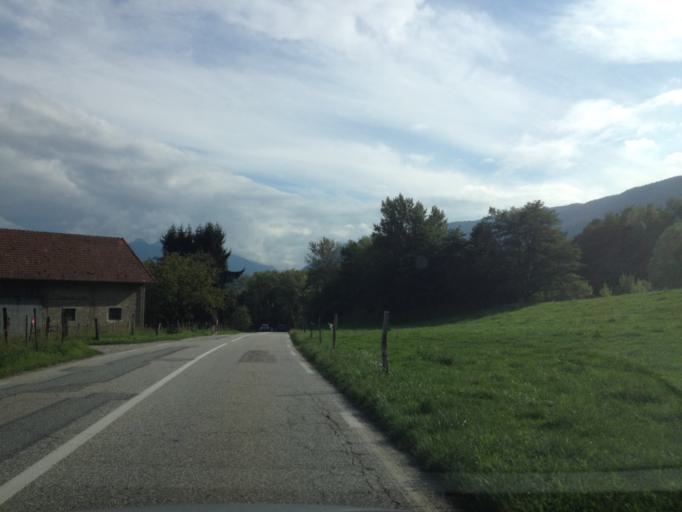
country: FR
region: Rhone-Alpes
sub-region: Departement de la Savoie
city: La Motte-Servolex
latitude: 45.6115
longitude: 5.8601
